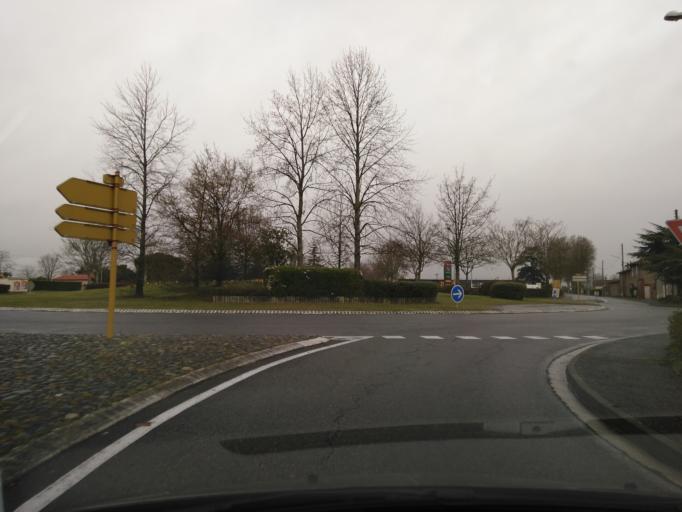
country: FR
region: Midi-Pyrenees
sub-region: Departement de la Haute-Garonne
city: Carbonne
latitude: 43.3015
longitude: 1.2204
